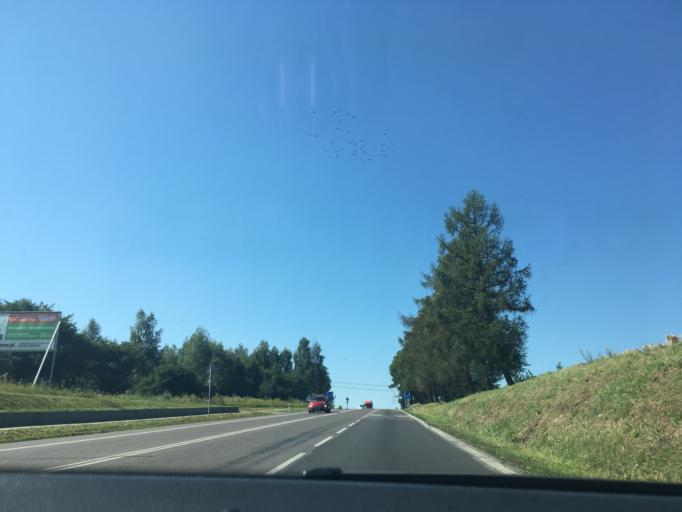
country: PL
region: Lublin Voivodeship
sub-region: Powiat lubelski
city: Jakubowice Murowane
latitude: 51.3144
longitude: 22.6031
